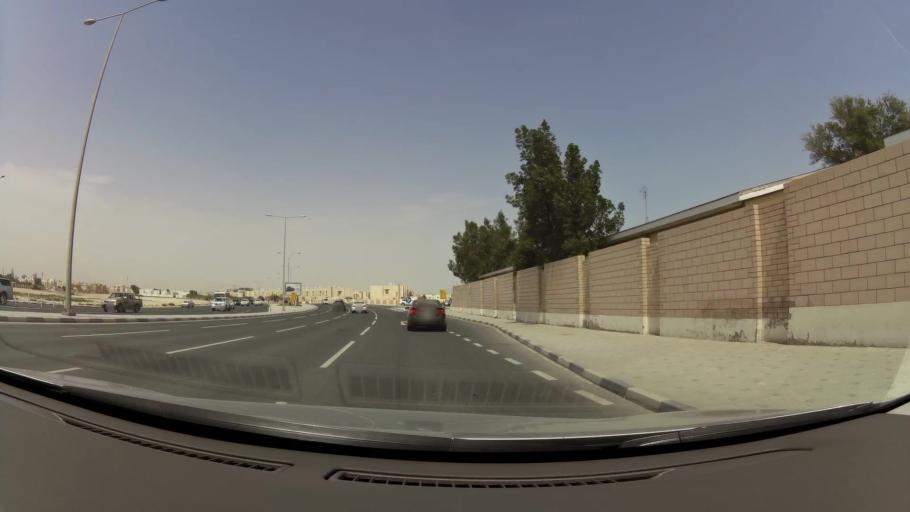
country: QA
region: Baladiyat ad Dawhah
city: Doha
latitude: 25.3241
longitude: 51.4866
